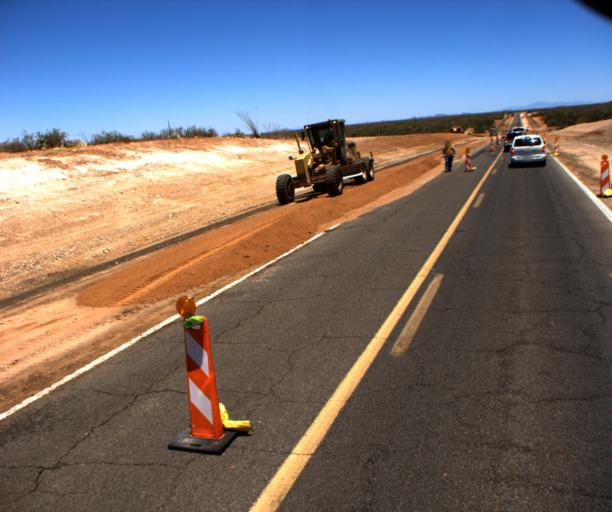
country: US
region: Arizona
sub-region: Pima County
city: Sells
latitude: 32.0004
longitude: -111.6891
